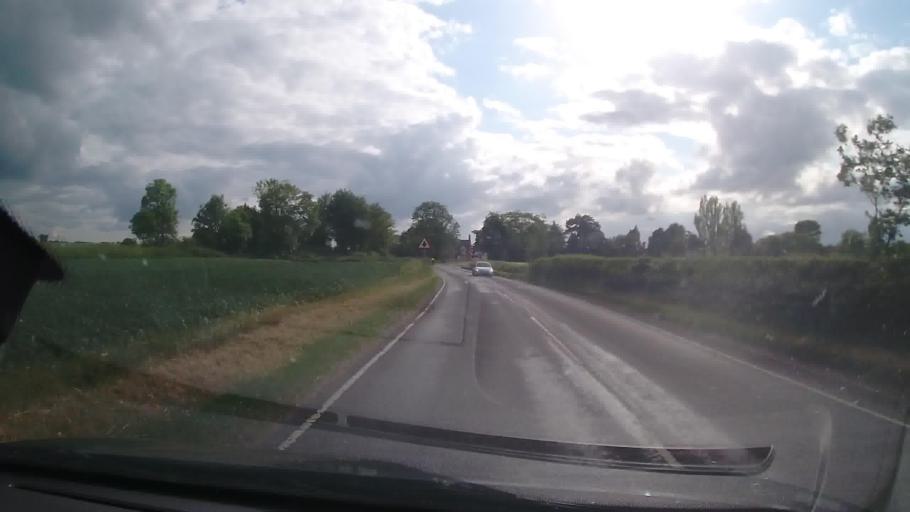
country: GB
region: England
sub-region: Shropshire
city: Withington
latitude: 52.7042
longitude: -2.5992
